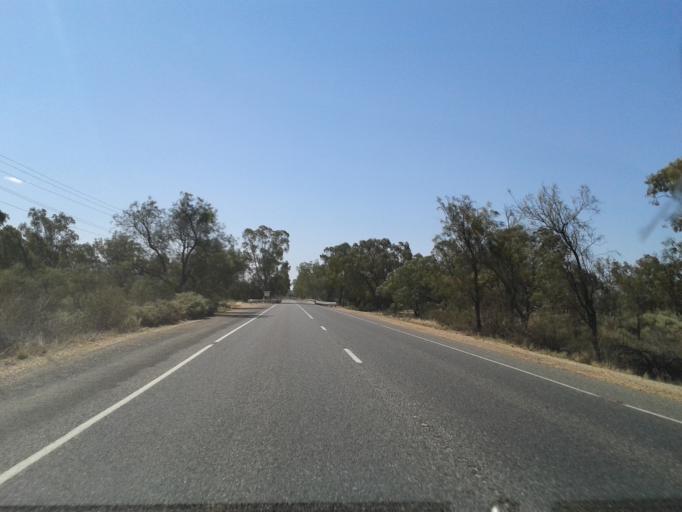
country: AU
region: South Australia
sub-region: Berri and Barmera
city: Berri
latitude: -34.3167
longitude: 140.6063
